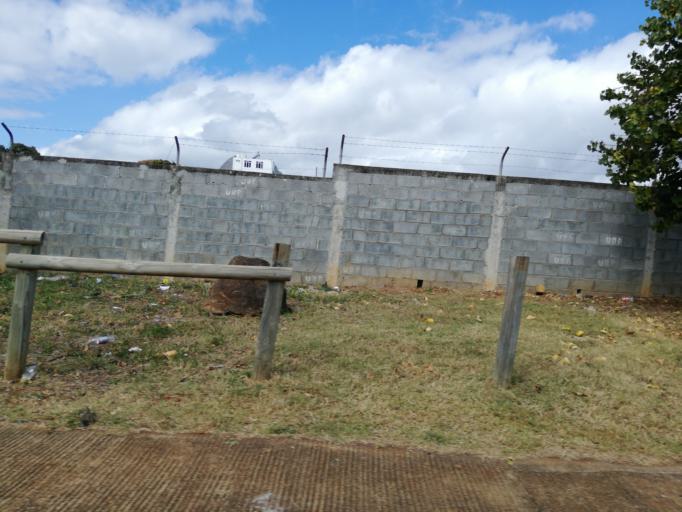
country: MU
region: Black River
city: Petite Riviere
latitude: -20.2152
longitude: 57.4639
